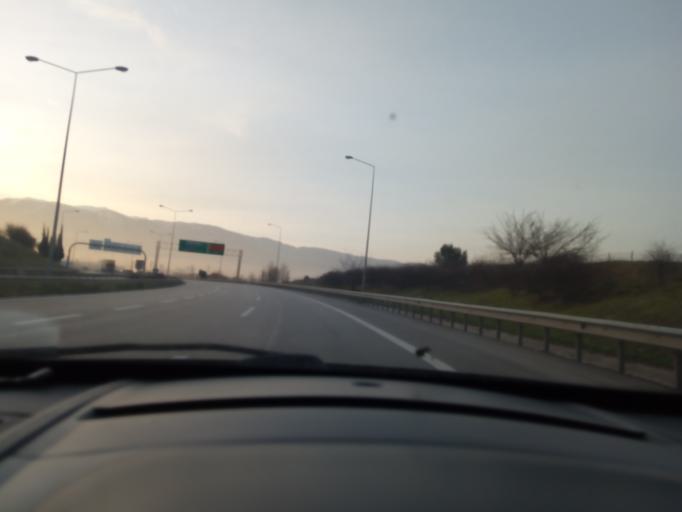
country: TR
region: Bursa
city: Demirtas
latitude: 40.2827
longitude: 29.0407
